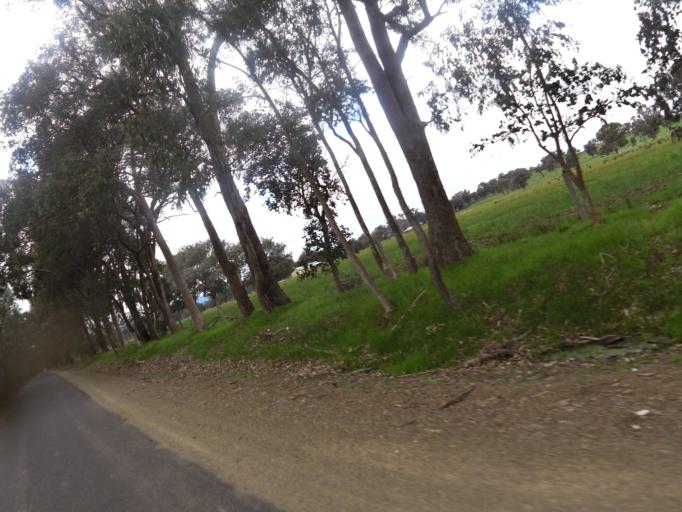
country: AU
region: Victoria
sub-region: Benalla
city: Benalla
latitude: -36.6792
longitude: 145.9654
